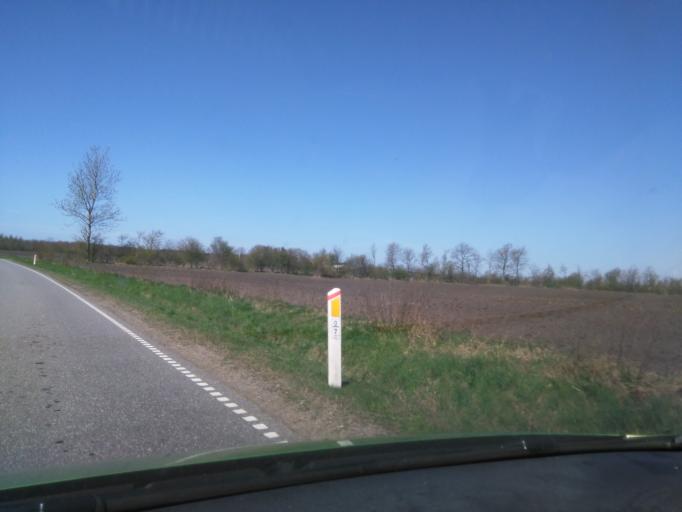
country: DK
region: South Denmark
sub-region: Billund Kommune
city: Grindsted
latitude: 55.7005
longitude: 8.8291
